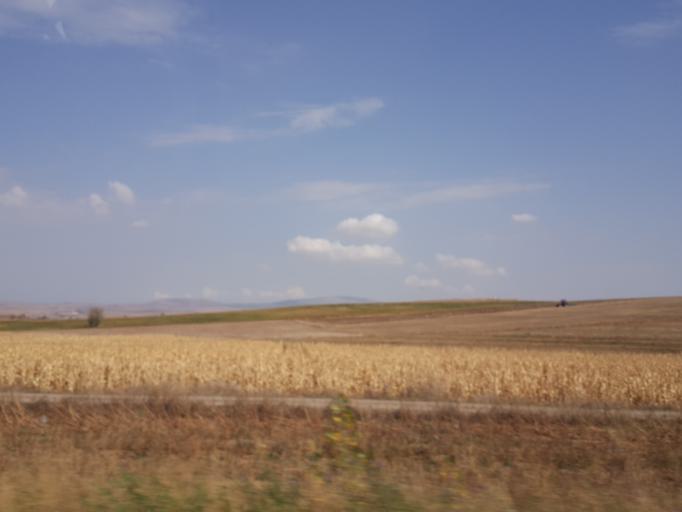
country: TR
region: Corum
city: Alaca
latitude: 40.1485
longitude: 34.8851
